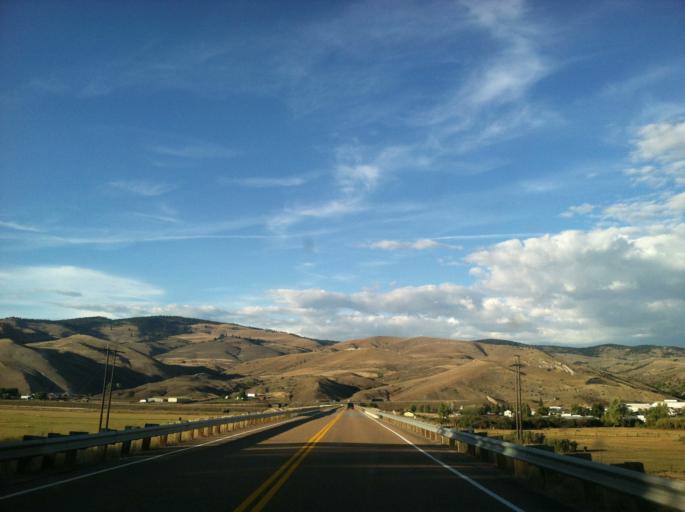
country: US
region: Montana
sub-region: Granite County
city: Philipsburg
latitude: 46.6647
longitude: -113.1557
